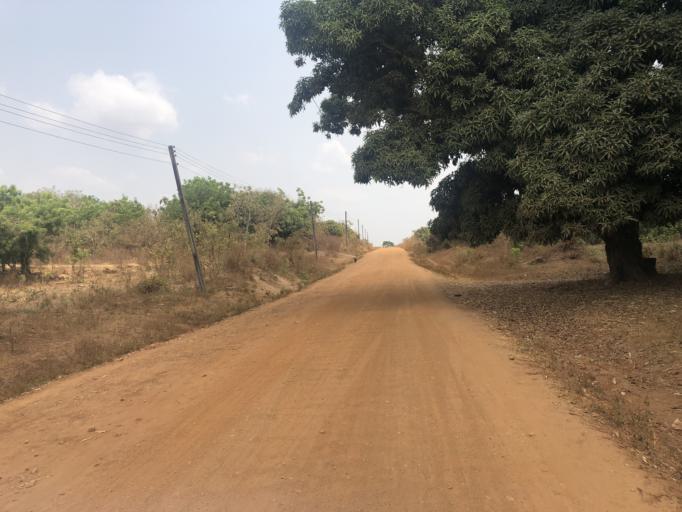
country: NG
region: Osun
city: Bode Osi
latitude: 7.8017
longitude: 4.1507
